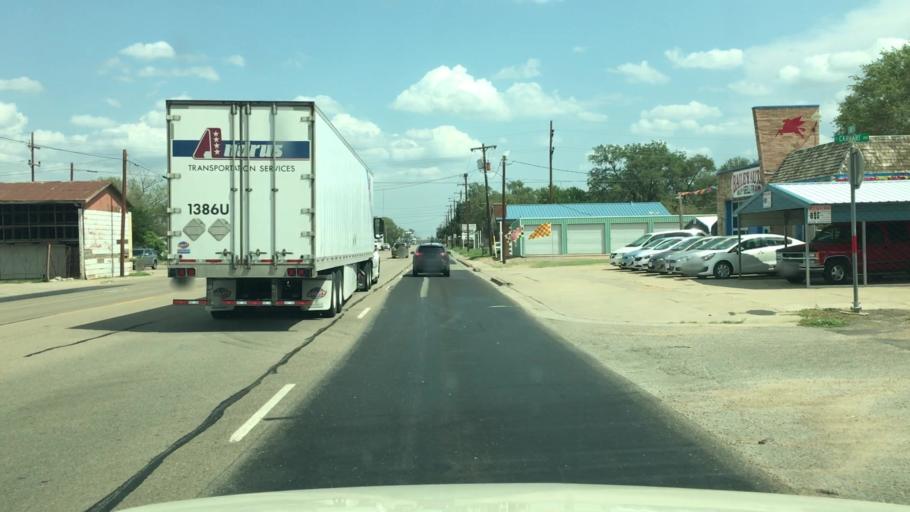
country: US
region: Texas
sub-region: Donley County
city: Clarendon
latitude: 34.9371
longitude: -100.8863
